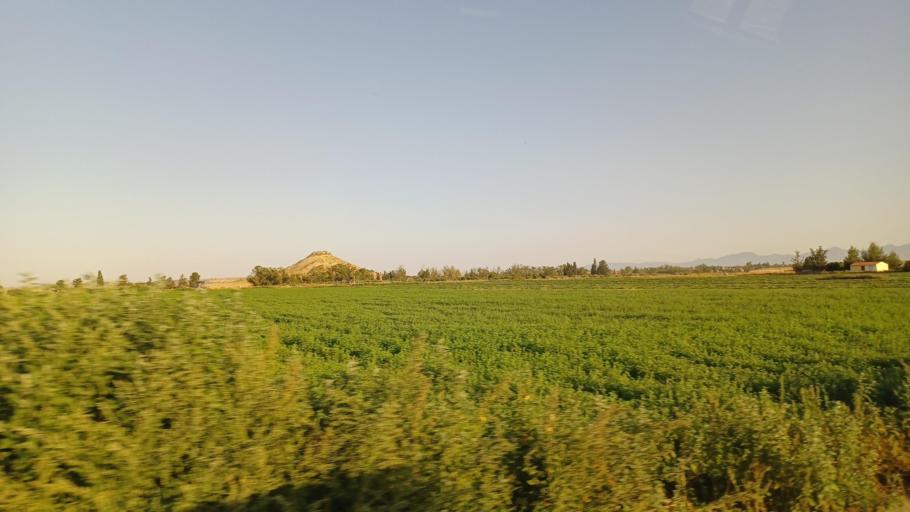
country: CY
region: Larnaka
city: Athienou
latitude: 35.0565
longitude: 33.5036
